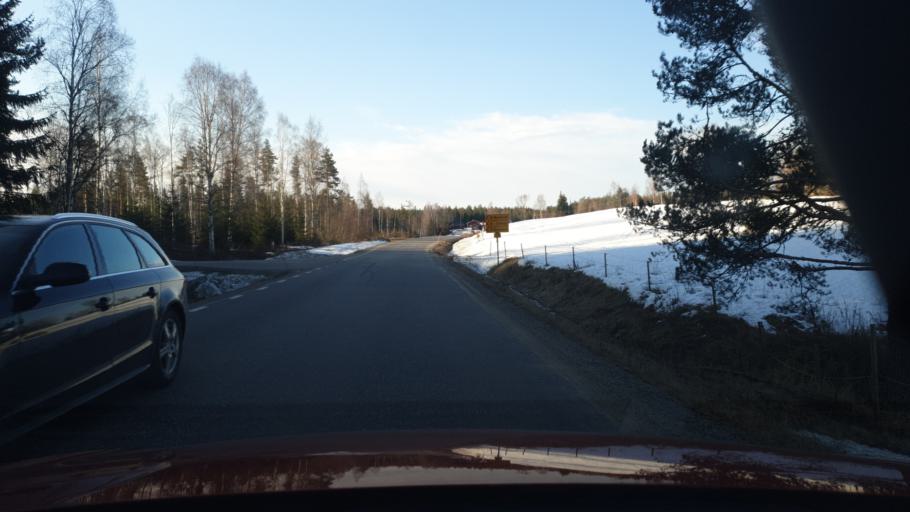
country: SE
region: Gaevleborg
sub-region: Ljusdals Kommun
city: Jaervsoe
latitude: 61.7699
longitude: 16.2131
